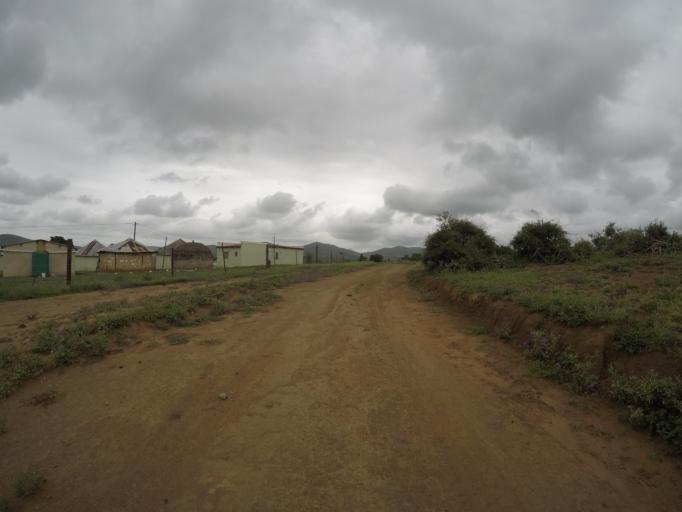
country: ZA
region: KwaZulu-Natal
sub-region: uThungulu District Municipality
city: Empangeni
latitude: -28.6027
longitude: 31.8642
